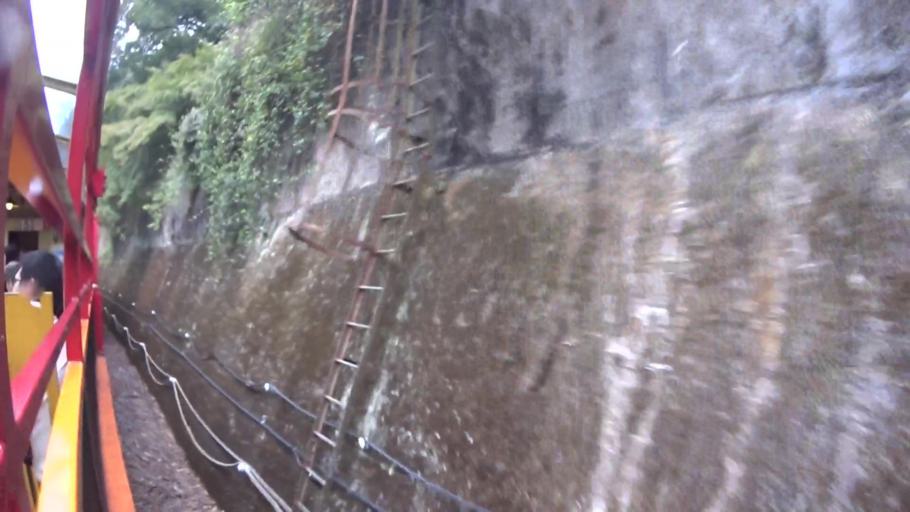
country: JP
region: Kyoto
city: Kameoka
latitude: 35.0256
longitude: 135.6554
